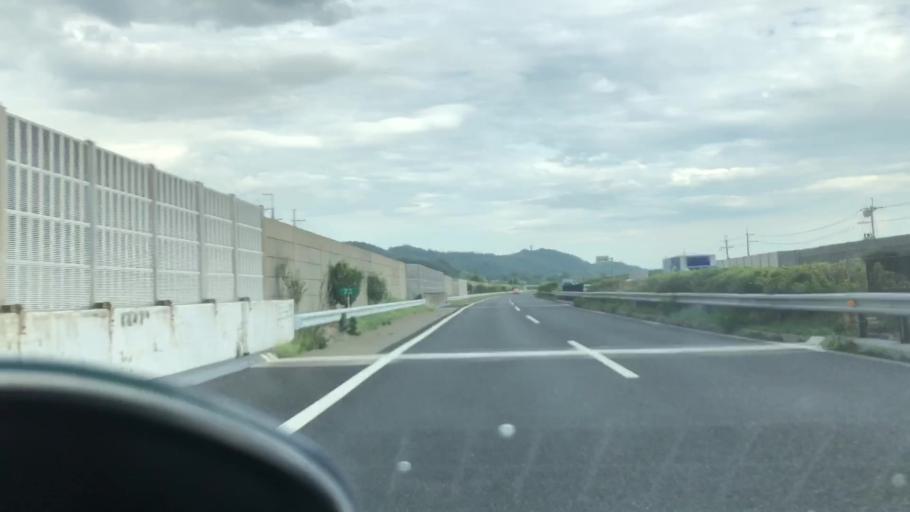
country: JP
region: Hyogo
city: Ono
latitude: 34.9389
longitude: 134.8287
